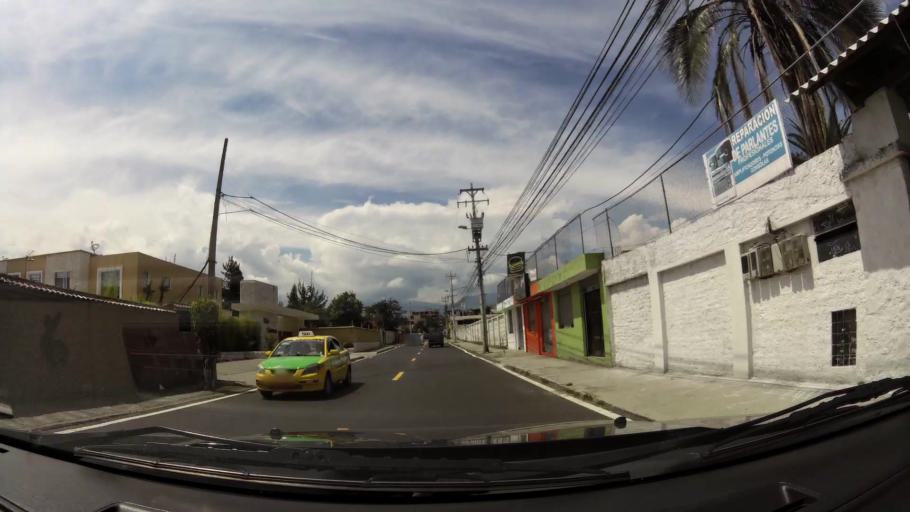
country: EC
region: Pichincha
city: Quito
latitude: -0.2110
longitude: -78.4085
